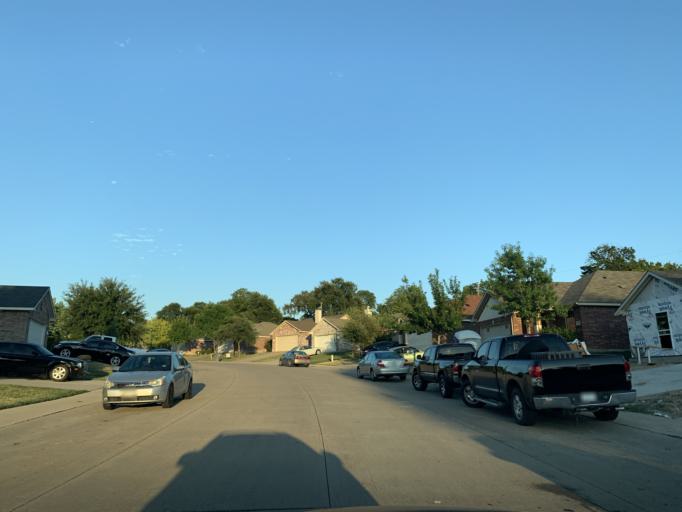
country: US
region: Texas
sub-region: Dallas County
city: Lancaster
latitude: 32.6675
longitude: -96.8013
